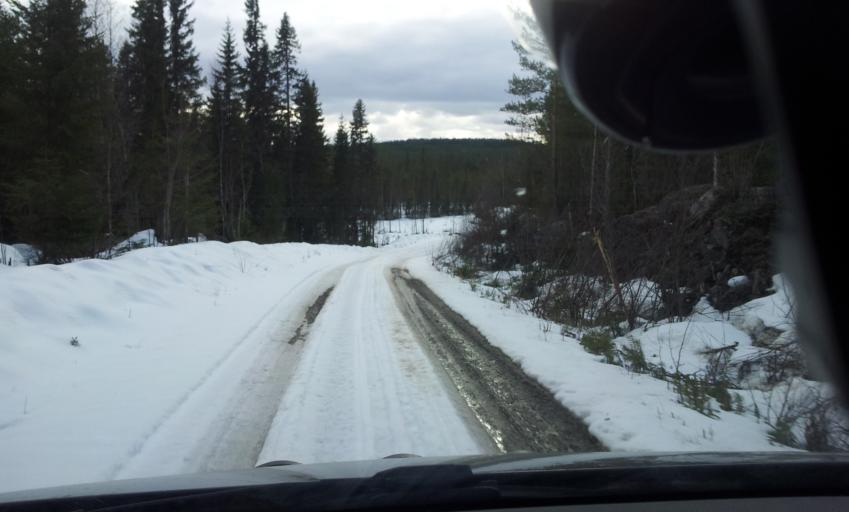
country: SE
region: Vaesternorrland
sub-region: Ange Kommun
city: Ange
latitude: 62.1912
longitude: 15.7771
